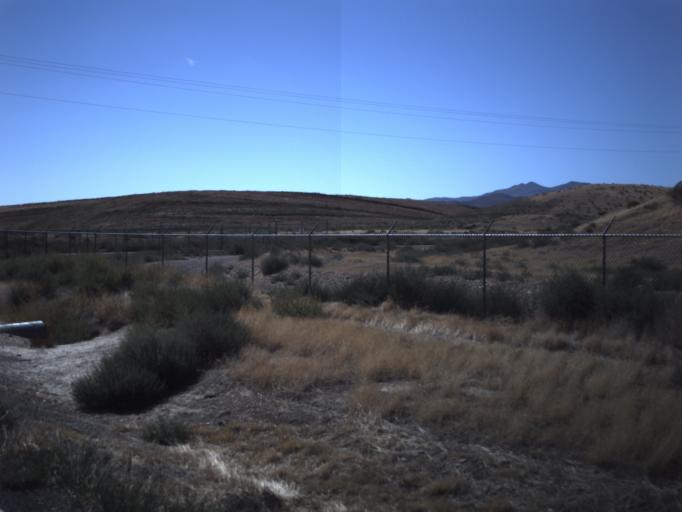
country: US
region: Utah
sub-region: Utah County
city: Genola
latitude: 40.0344
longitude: -111.9584
